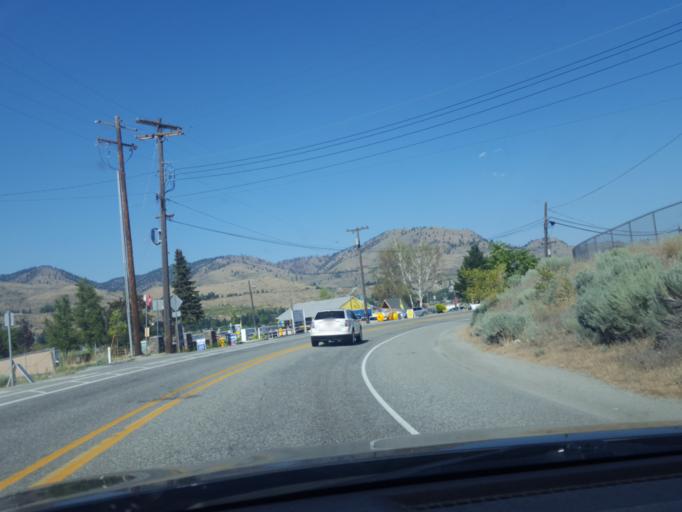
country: US
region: Washington
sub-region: Chelan County
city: Chelan
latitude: 47.8356
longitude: -120.0379
